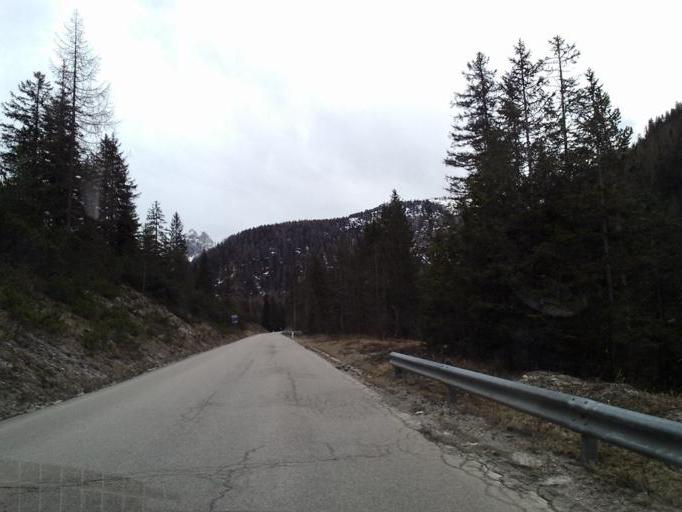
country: IT
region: Veneto
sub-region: Provincia di Belluno
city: Cortina d'Ampezzo
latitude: 46.6075
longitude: 12.2359
